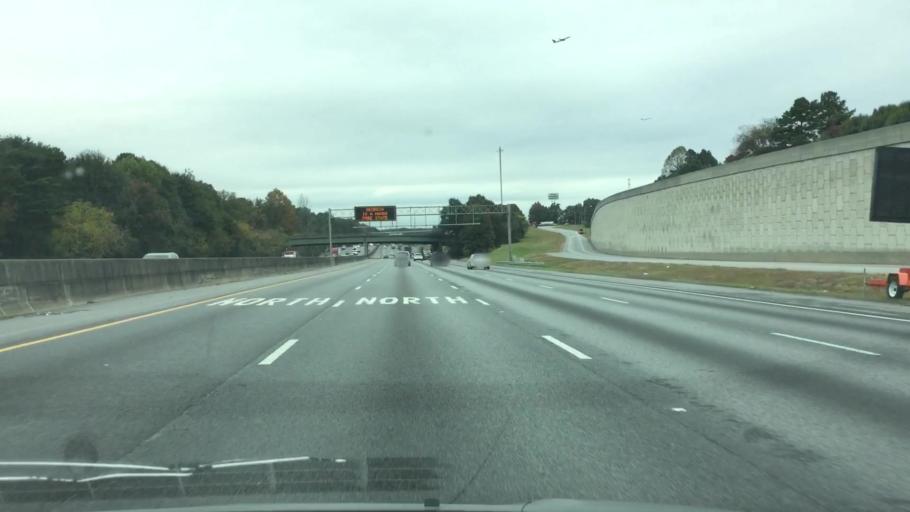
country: US
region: Georgia
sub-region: Clayton County
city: Forest Park
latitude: 33.6123
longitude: -84.3968
